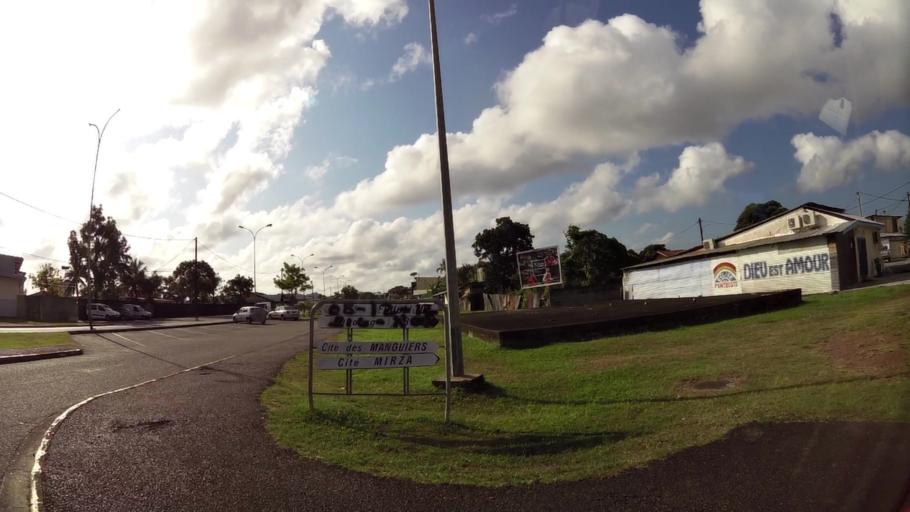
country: GF
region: Guyane
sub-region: Guyane
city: Cayenne
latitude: 4.9372
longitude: -52.3221
